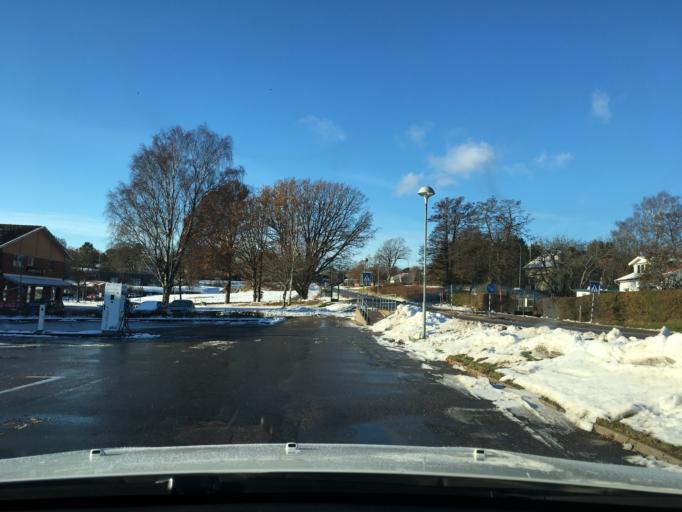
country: SE
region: Vaestra Goetaland
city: Svanesund
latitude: 58.1429
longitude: 11.8209
